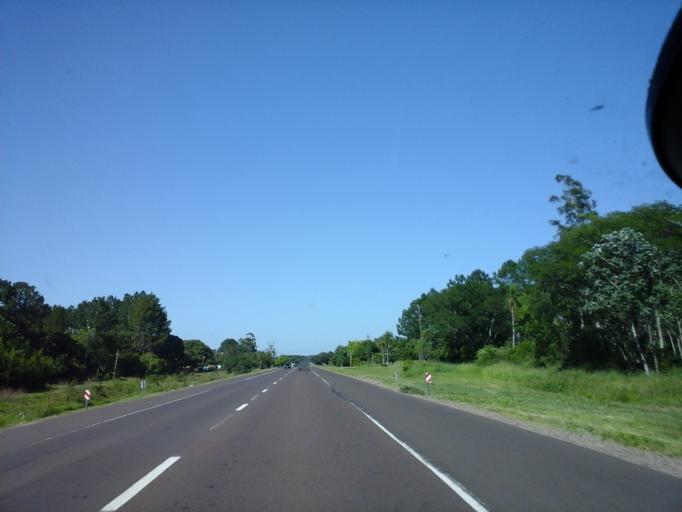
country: AR
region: Corrientes
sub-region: Departamento de San Cosme
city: San Cosme
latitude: -27.3879
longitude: -58.5465
